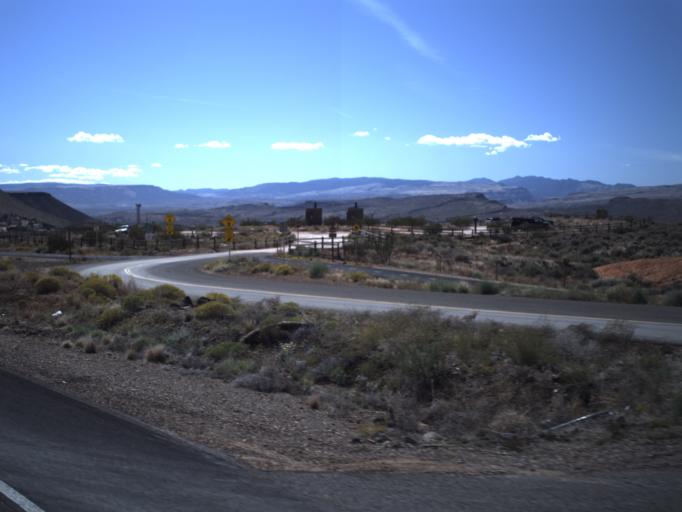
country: US
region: Utah
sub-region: Washington County
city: Saint George
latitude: 37.1394
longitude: -113.6040
